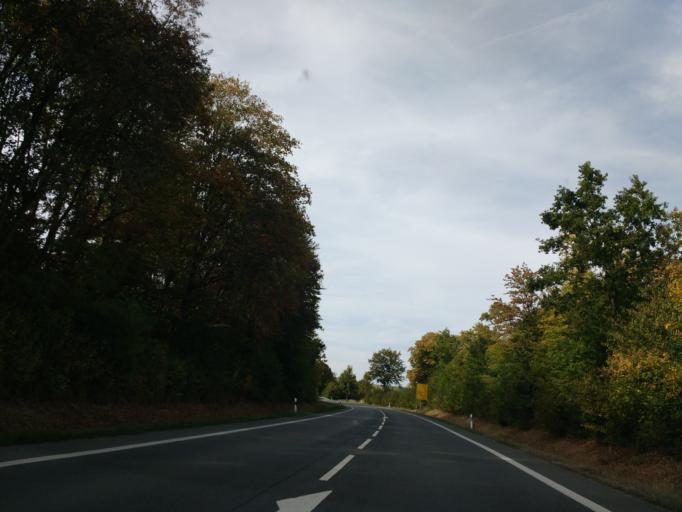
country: DE
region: North Rhine-Westphalia
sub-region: Regierungsbezirk Detmold
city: Willebadessen
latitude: 51.6259
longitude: 9.1387
